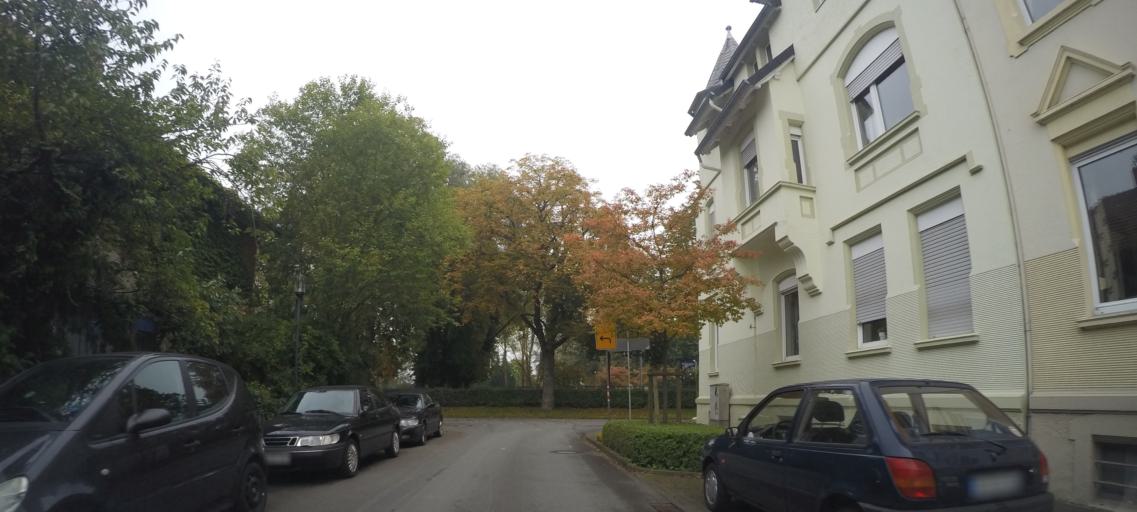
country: DE
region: North Rhine-Westphalia
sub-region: Regierungsbezirk Arnsberg
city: Lippstadt
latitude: 51.6755
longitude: 8.3357
